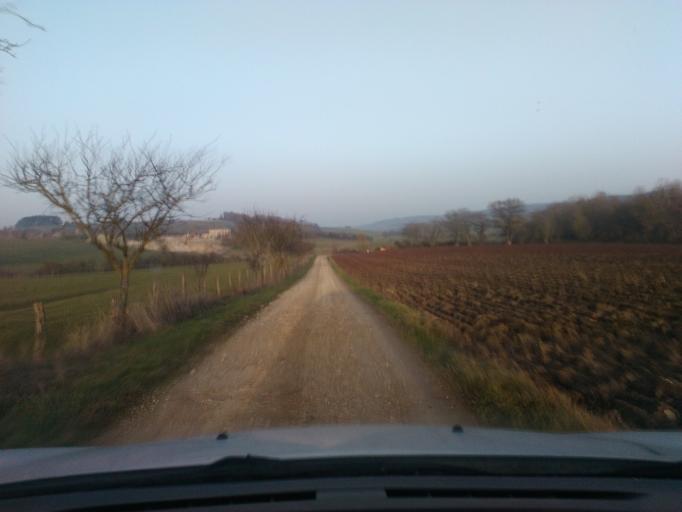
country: FR
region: Lorraine
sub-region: Departement des Vosges
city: Vittel
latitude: 48.2644
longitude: 6.0212
